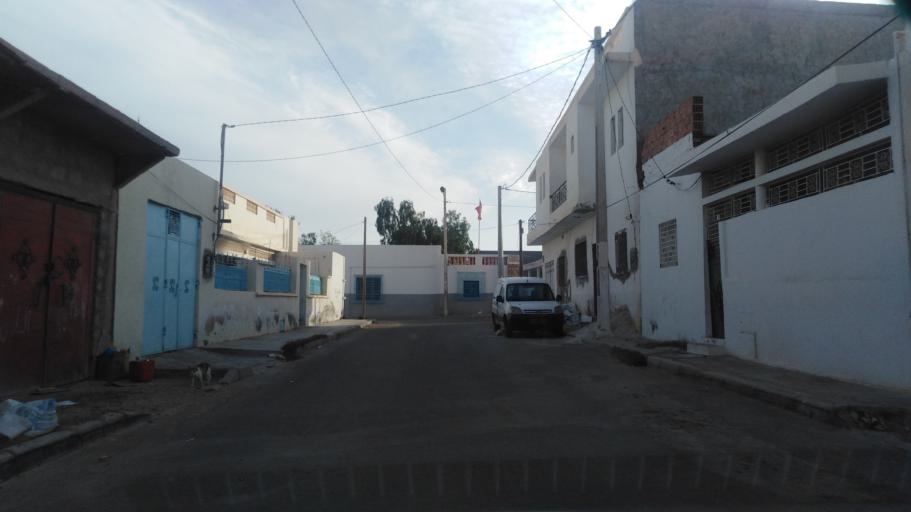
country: TN
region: Tataouine
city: Tataouine
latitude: 32.9364
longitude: 10.4558
